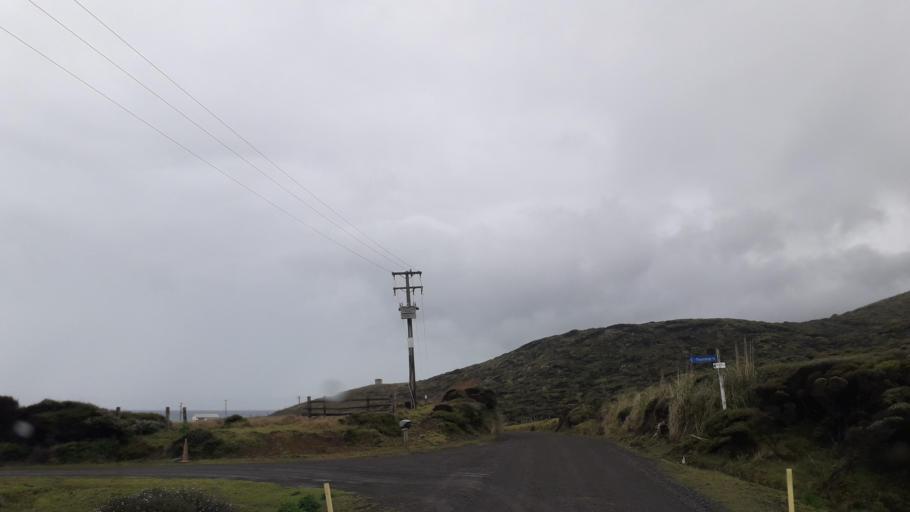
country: NZ
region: Northland
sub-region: Far North District
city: Ahipara
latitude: -35.4313
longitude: 173.2778
